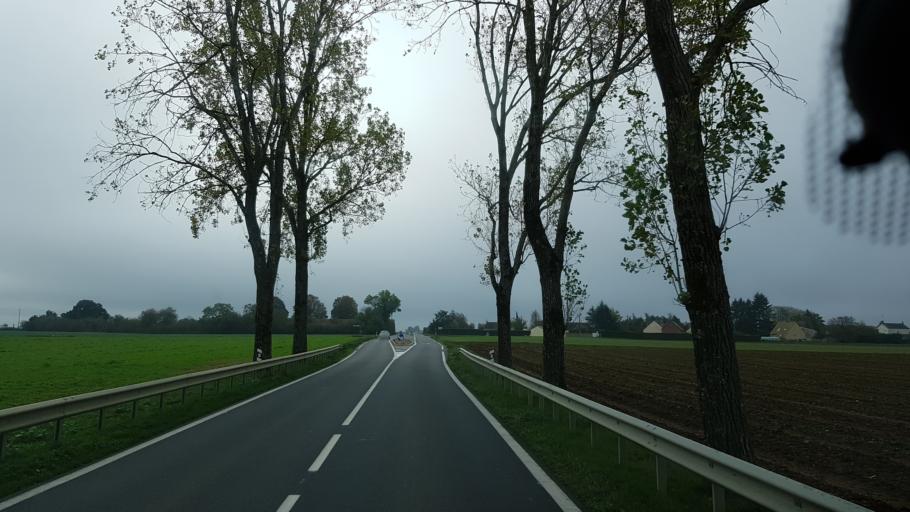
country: FR
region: Ile-de-France
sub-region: Departement de l'Essonne
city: Corbreuse
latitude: 48.4261
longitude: 1.9627
